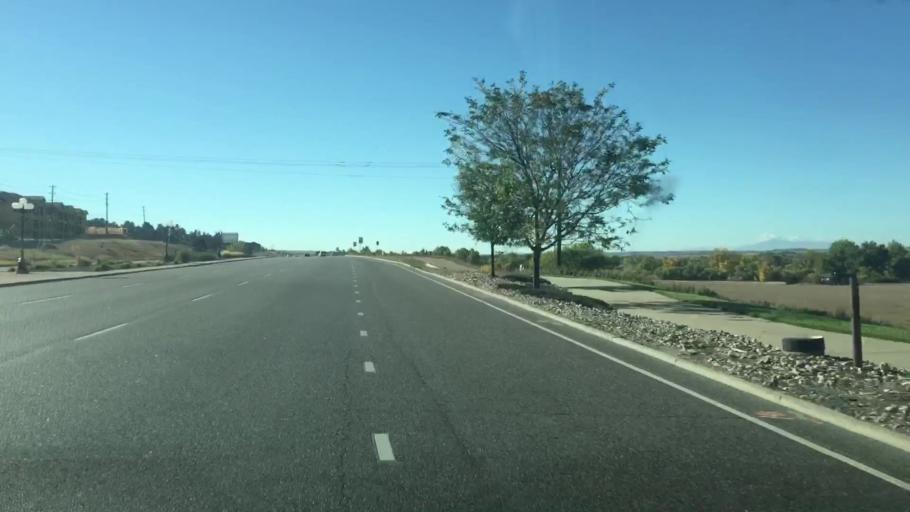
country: US
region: Colorado
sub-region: Douglas County
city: Parker
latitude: 39.5083
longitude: -104.7636
